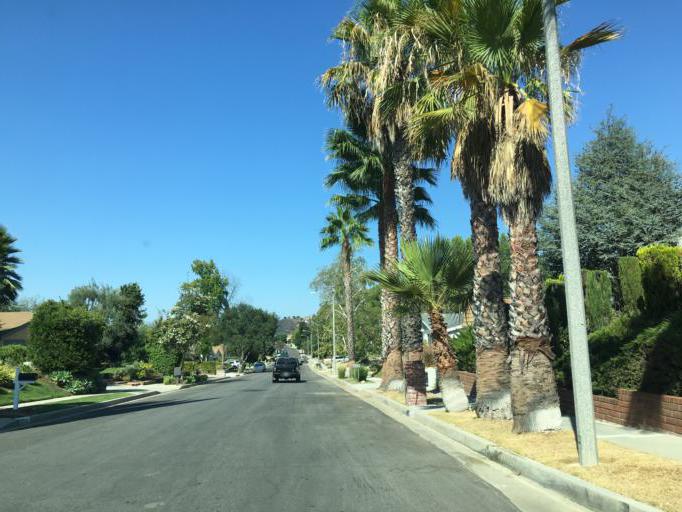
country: US
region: California
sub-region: Los Angeles County
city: Woodland Hills
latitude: 34.1361
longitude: -118.5936
